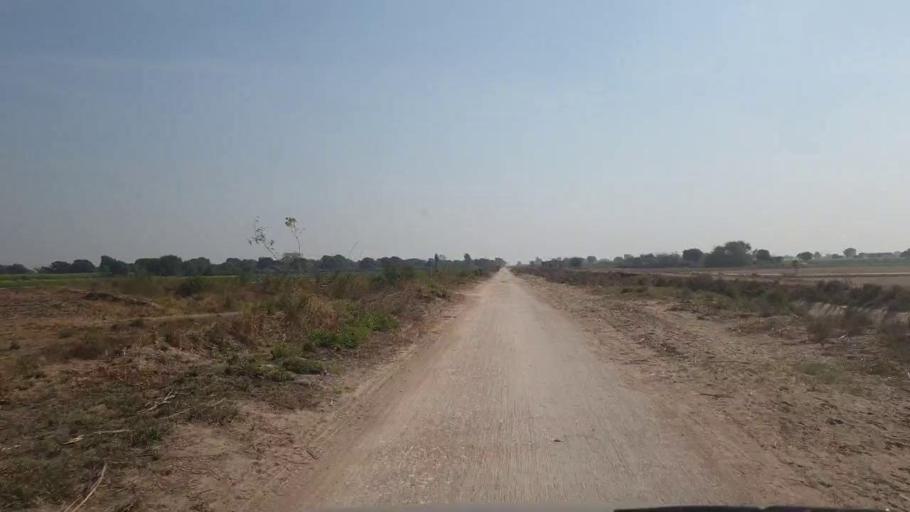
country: PK
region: Sindh
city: Chambar
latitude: 25.3621
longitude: 68.7988
